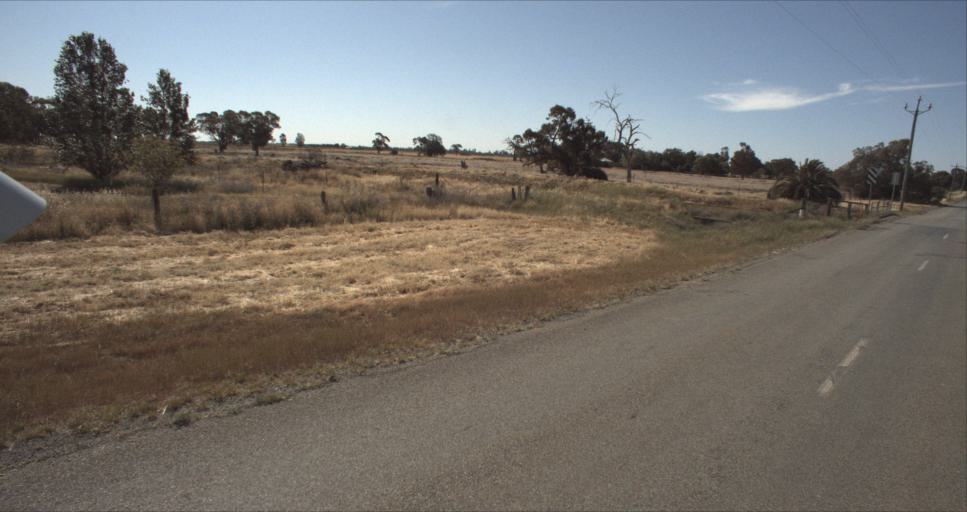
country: AU
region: New South Wales
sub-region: Leeton
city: Leeton
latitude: -34.5701
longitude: 146.3818
